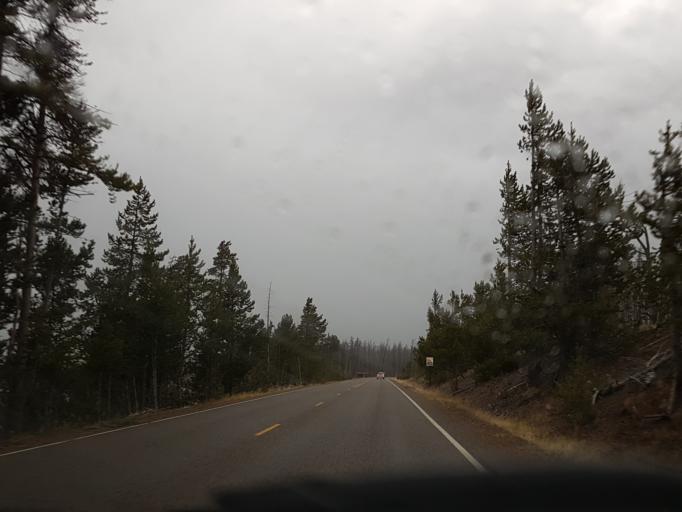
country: US
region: Montana
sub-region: Gallatin County
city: West Yellowstone
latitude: 44.4718
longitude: -110.5227
